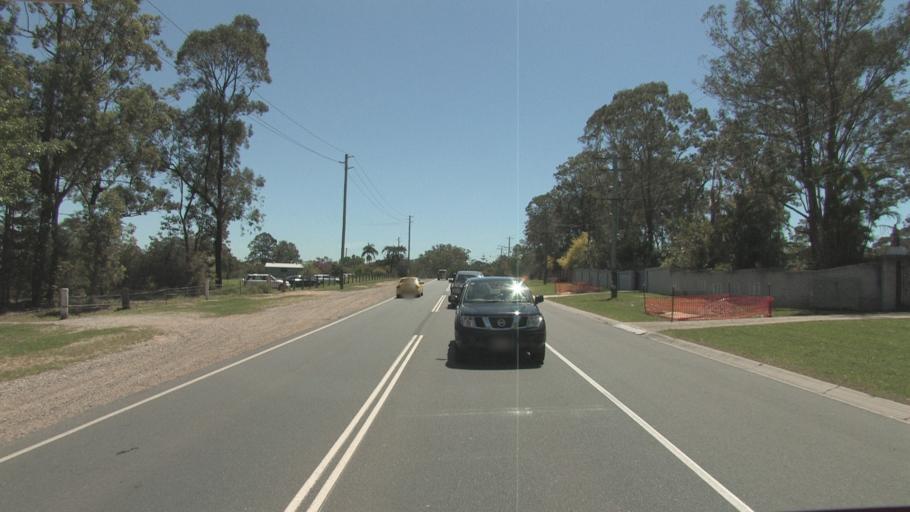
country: AU
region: Queensland
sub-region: Logan
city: Park Ridge South
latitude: -27.7038
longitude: 153.0090
